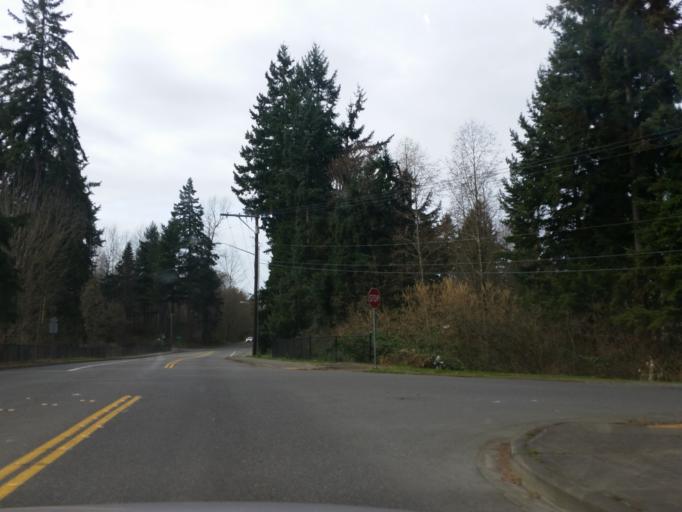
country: US
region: Washington
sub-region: Pierce County
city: McMillin
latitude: 47.1457
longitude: -122.2530
